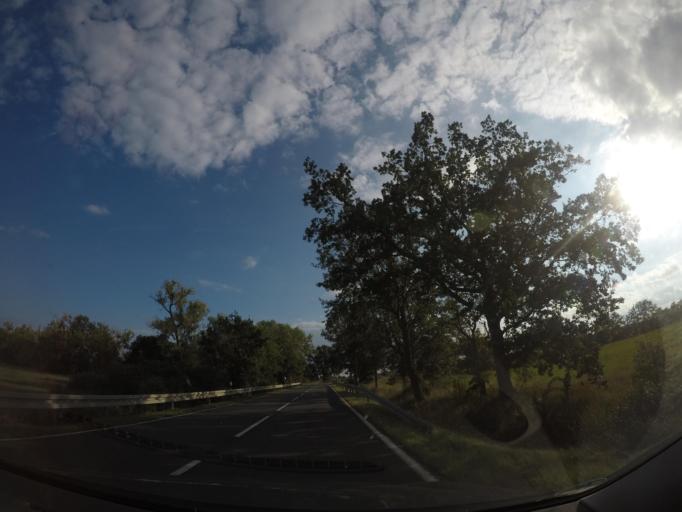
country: DE
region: Saxony-Anhalt
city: Weferlingen
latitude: 52.3779
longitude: 11.1017
